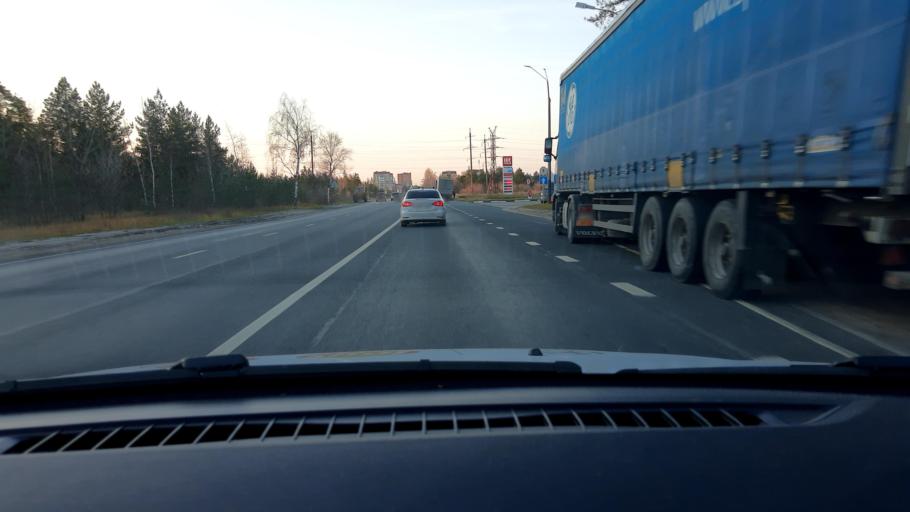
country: RU
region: Nizjnij Novgorod
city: Dzerzhinsk
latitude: 56.2632
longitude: 43.4690
